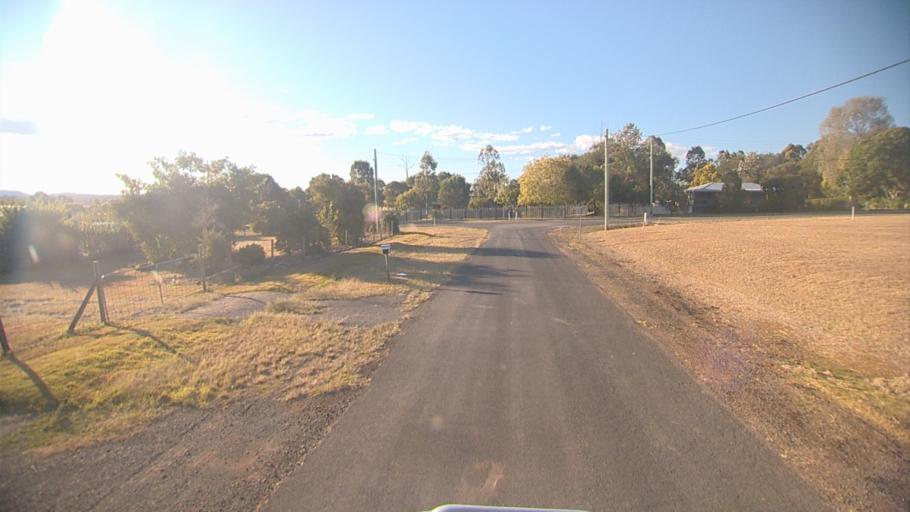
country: AU
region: Queensland
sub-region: Logan
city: Cedar Vale
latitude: -27.8631
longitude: 152.9694
